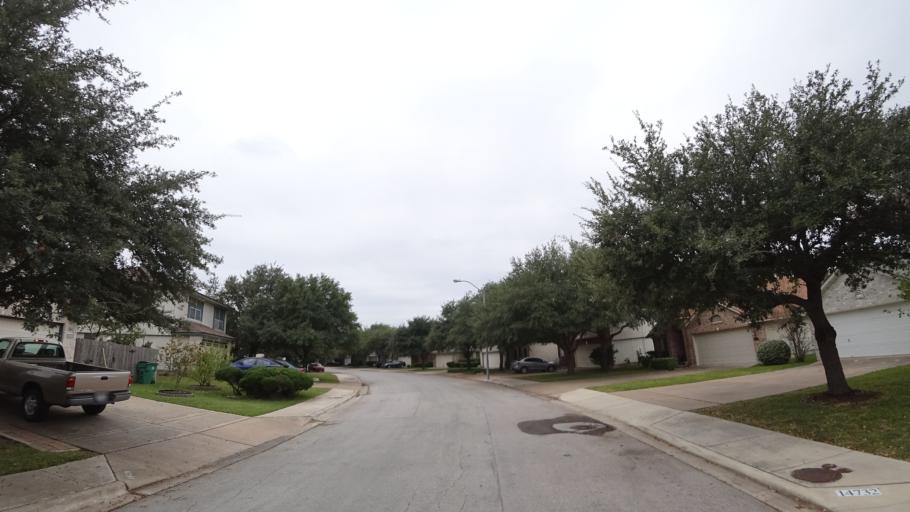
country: US
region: Texas
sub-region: Travis County
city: Wells Branch
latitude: 30.4491
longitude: -97.6901
